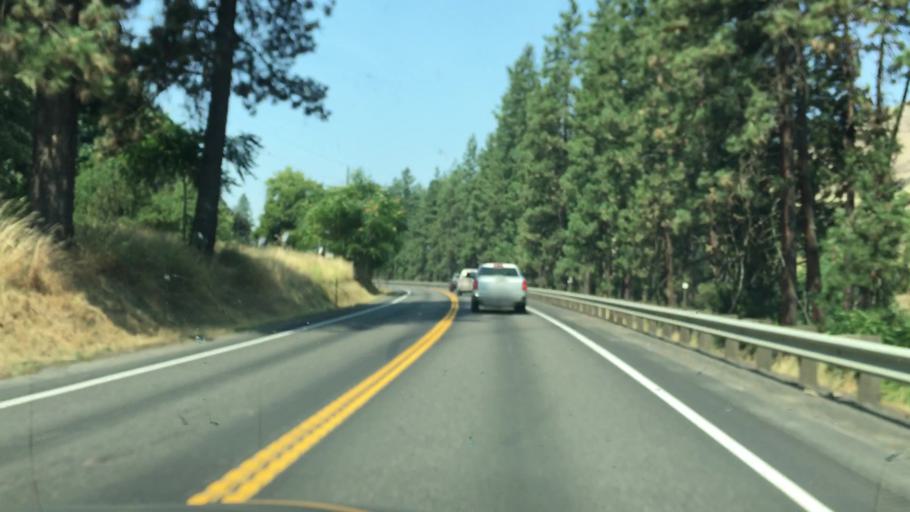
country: US
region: Idaho
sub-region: Clearwater County
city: Orofino
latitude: 46.4997
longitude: -116.4729
